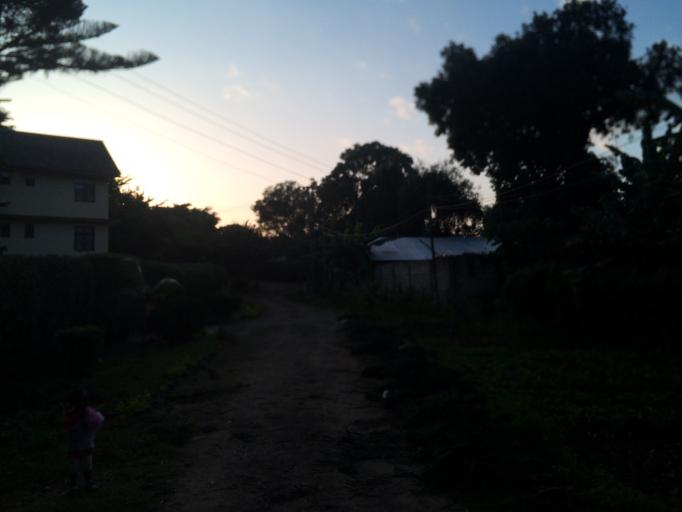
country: TZ
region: Arusha
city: Arusha
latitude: -3.3648
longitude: 36.6986
